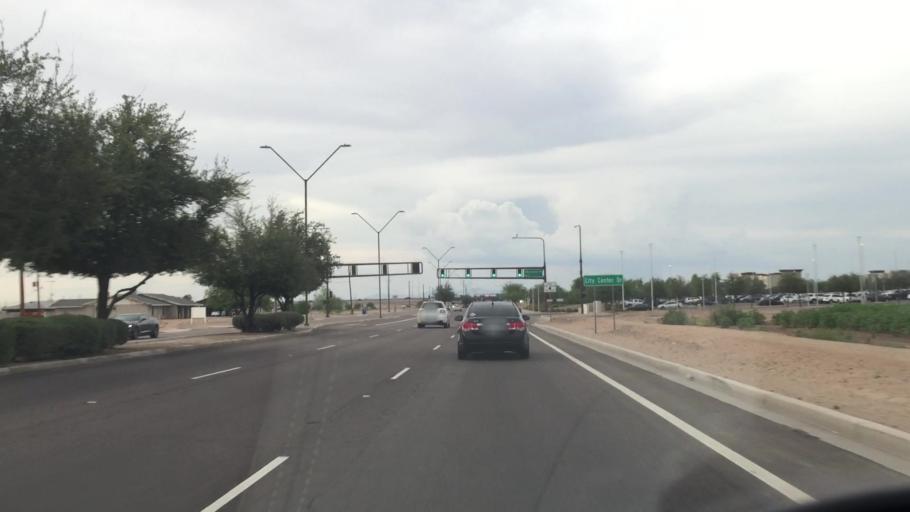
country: US
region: Arizona
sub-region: Maricopa County
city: Avondale
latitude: 33.4516
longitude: -112.3063
